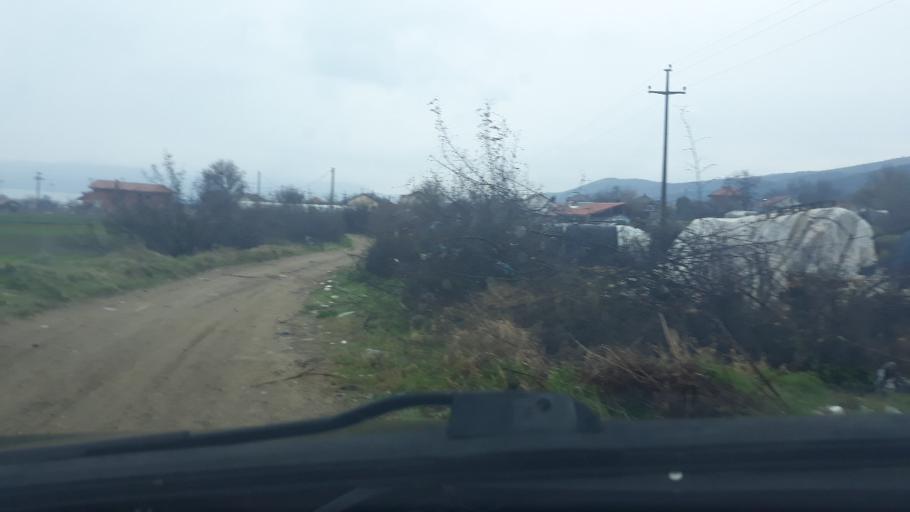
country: MK
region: Dojran
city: Star Dojran
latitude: 41.2650
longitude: 22.7515
